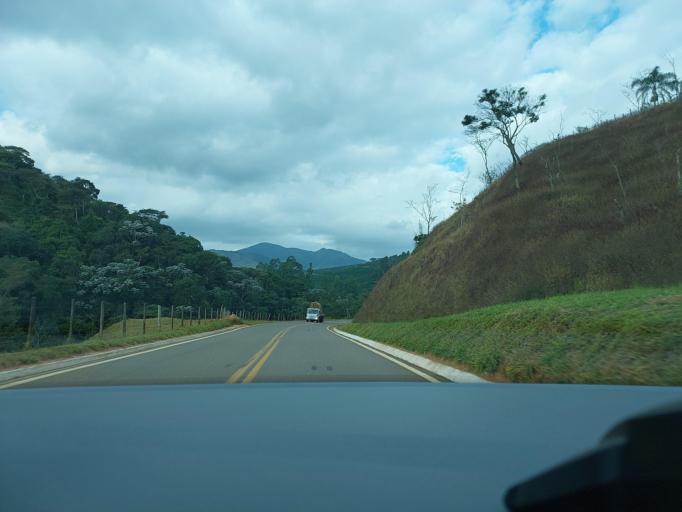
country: BR
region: Minas Gerais
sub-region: Visconde Do Rio Branco
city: Visconde do Rio Branco
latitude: -20.9359
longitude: -42.6307
